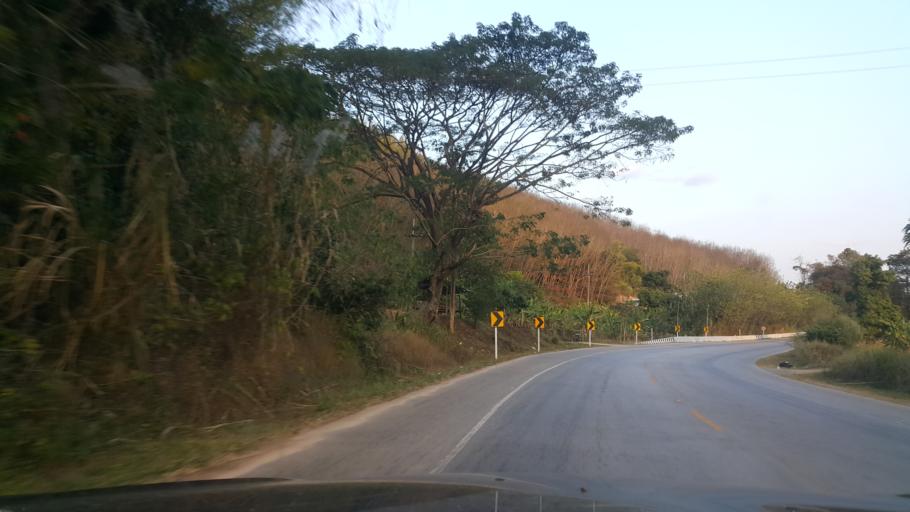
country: TH
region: Loei
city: Loei
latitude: 17.4755
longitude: 101.5656
